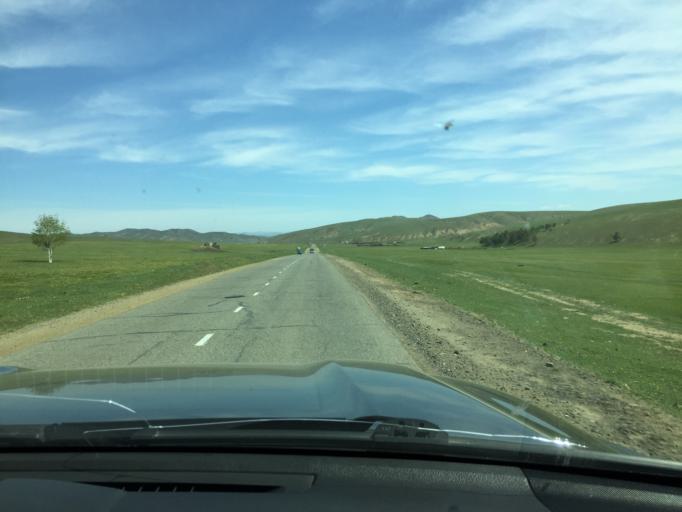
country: MN
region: Central Aimak
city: Javhlant
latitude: 48.6581
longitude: 106.1176
